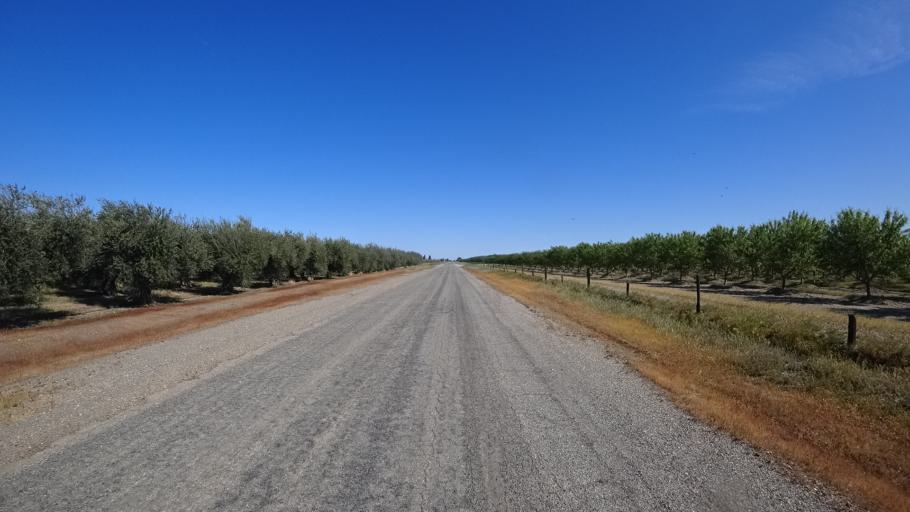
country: US
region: California
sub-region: Glenn County
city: Willows
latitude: 39.6296
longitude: -122.1600
